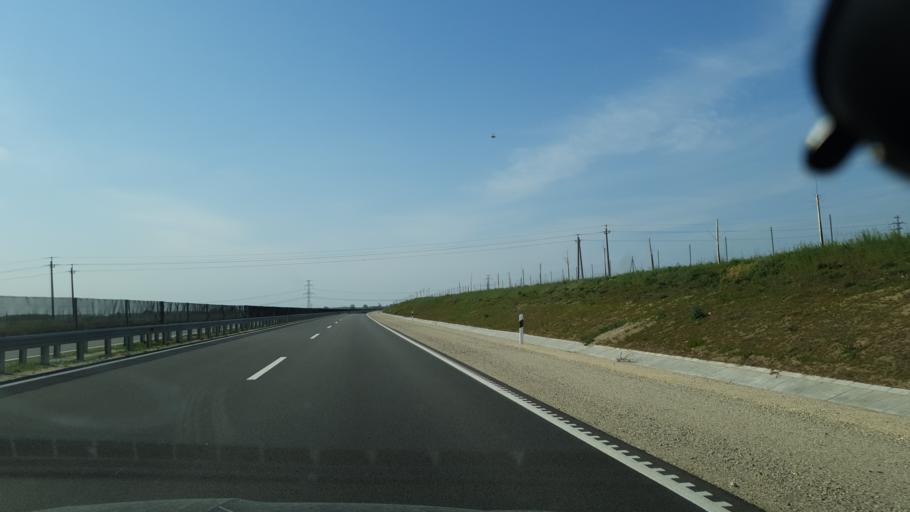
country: HU
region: Pest
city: Albertirsa
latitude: 47.2756
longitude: 19.5984
